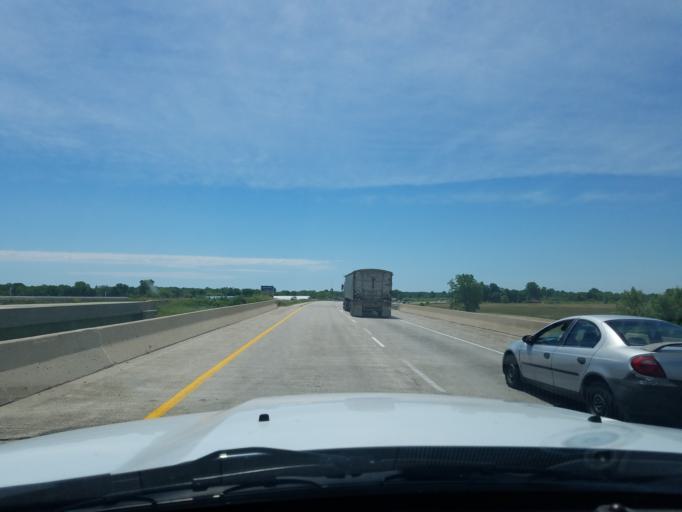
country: US
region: Indiana
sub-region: Delaware County
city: Muncie
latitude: 40.2130
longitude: -85.3374
